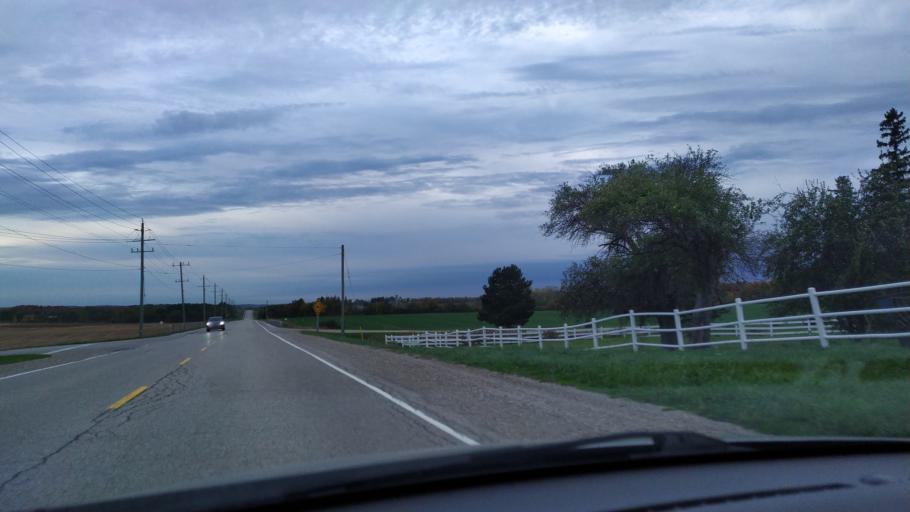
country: CA
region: Ontario
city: Stratford
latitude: 43.4967
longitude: -80.7675
